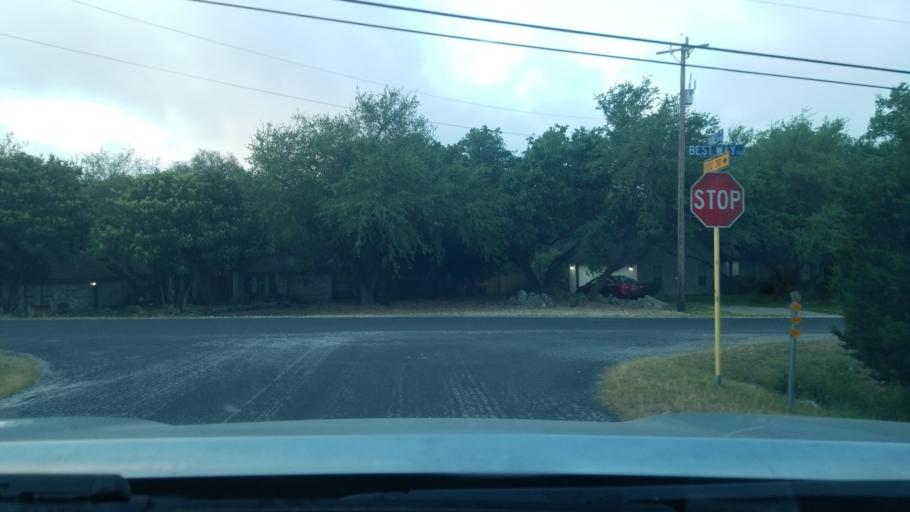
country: US
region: Texas
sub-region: Bexar County
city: Timberwood Park
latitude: 29.6973
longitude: -98.5044
